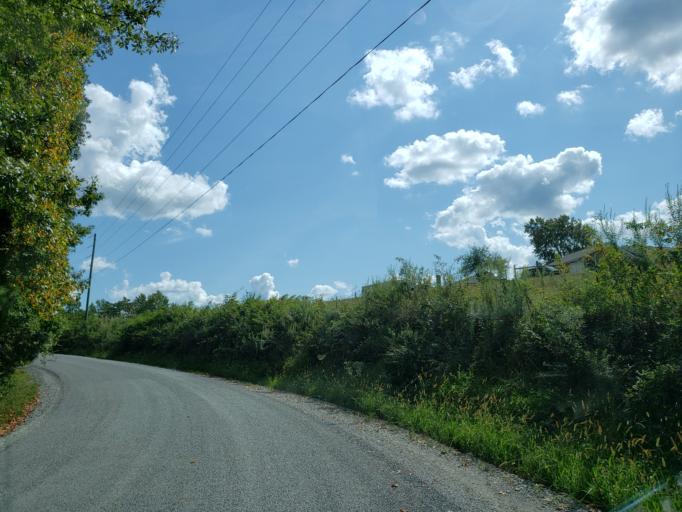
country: US
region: Georgia
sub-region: Pickens County
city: Jasper
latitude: 34.4288
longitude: -84.4557
